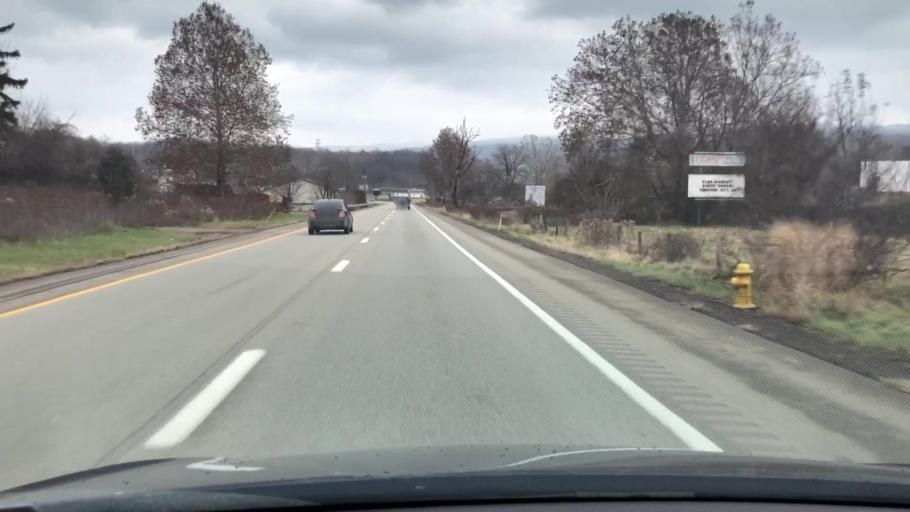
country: US
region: Pennsylvania
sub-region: Fayette County
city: Dunbar
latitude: 39.9935
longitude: -79.6158
